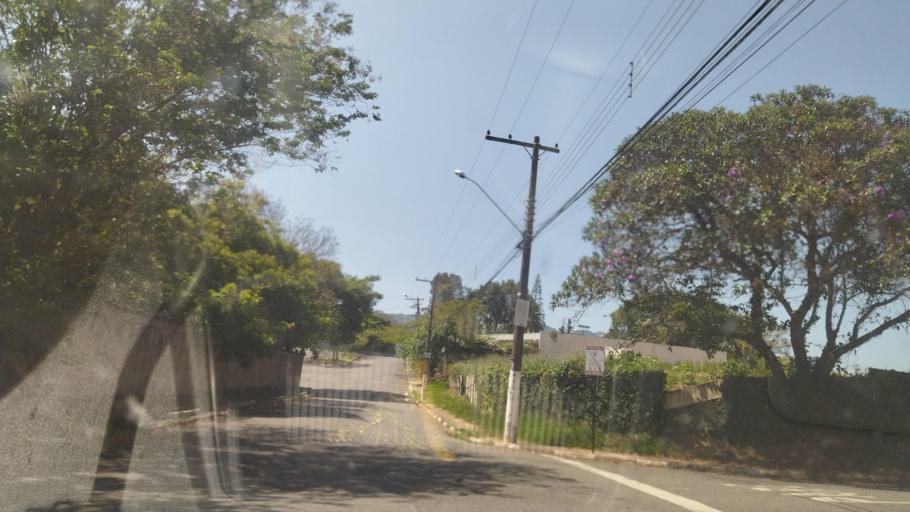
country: BR
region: Sao Paulo
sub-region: Atibaia
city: Atibaia
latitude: -23.1262
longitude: -46.5457
